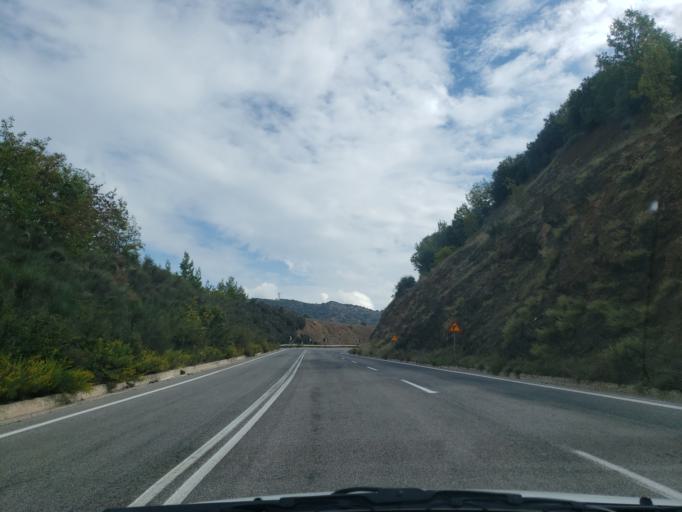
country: GR
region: Central Greece
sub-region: Nomos Fthiotidos
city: Stavros
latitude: 38.9992
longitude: 22.3690
